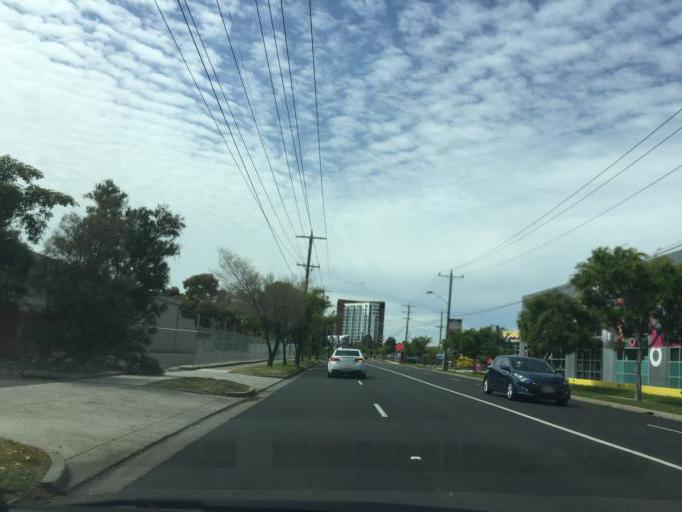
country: AU
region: Victoria
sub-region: Maribyrnong
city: Maidstone
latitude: -37.7777
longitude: 144.8768
